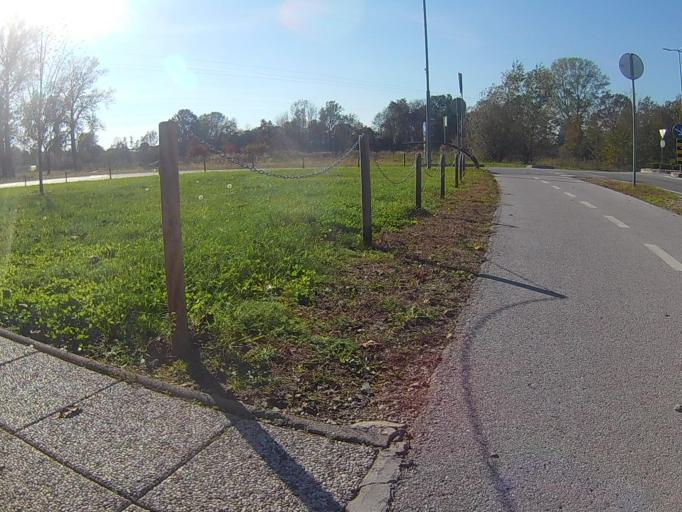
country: SI
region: Hajdina
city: Spodnja Hajdina
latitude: 46.4321
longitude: 15.8313
